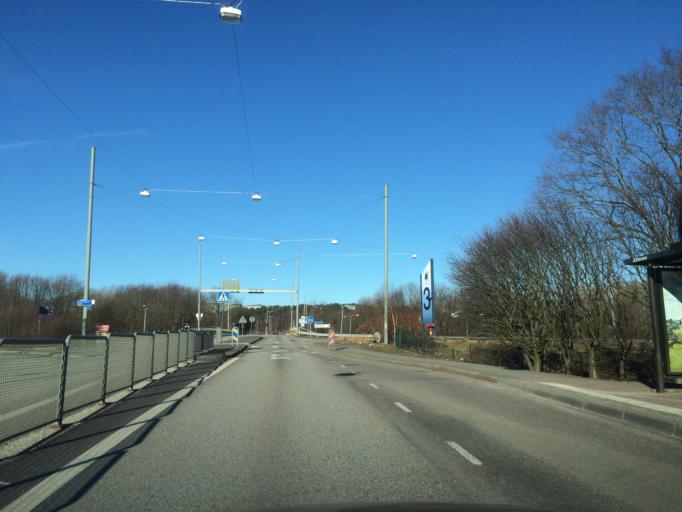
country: SE
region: Vaestra Goetaland
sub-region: Goteborg
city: Majorna
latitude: 57.6489
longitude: 11.9349
